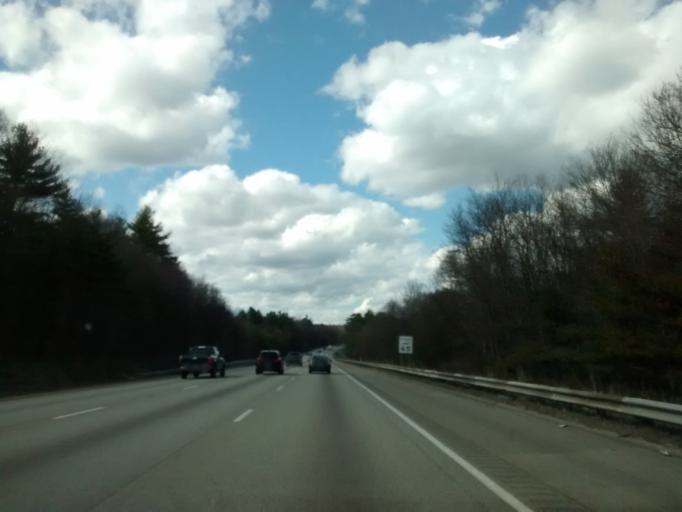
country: US
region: Massachusetts
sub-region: Middlesex County
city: Hopkinton
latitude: 42.2247
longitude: -71.5485
